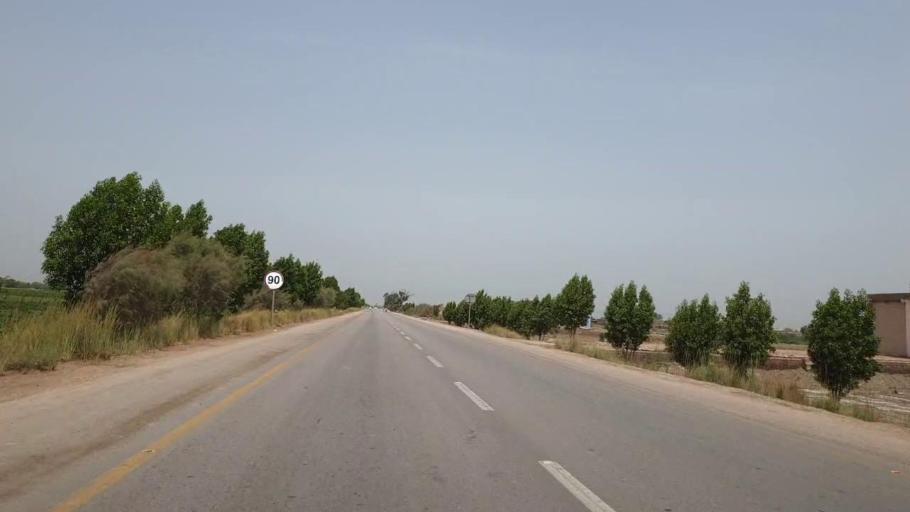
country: PK
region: Sindh
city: Nawabshah
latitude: 26.2248
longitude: 68.4938
